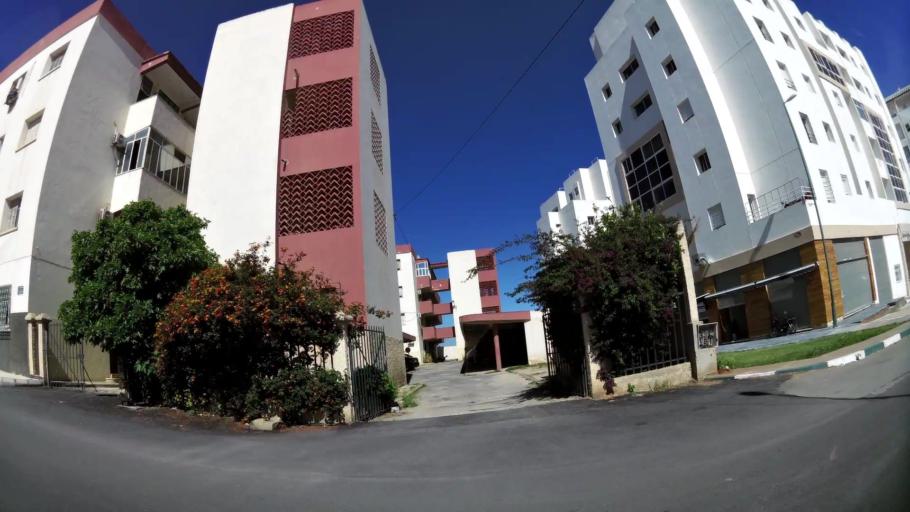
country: MA
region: Meknes-Tafilalet
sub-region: Meknes
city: Meknes
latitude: 33.9055
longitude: -5.5464
